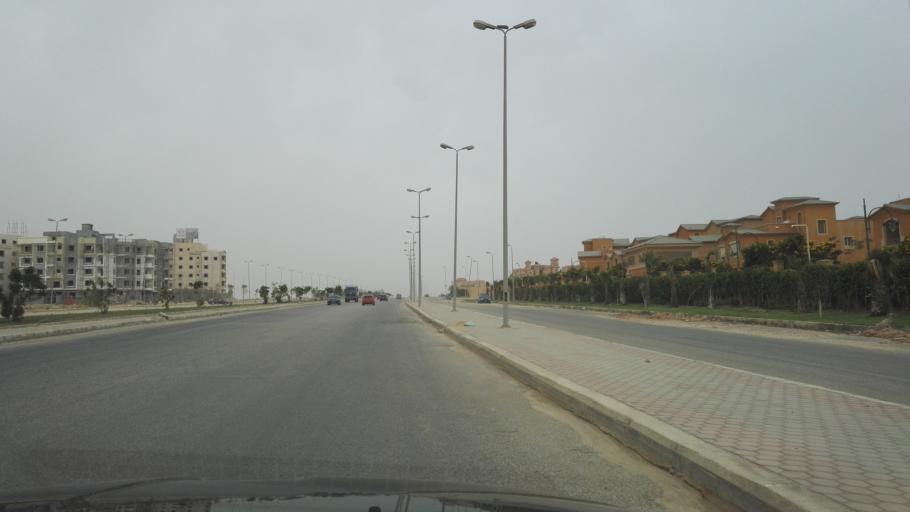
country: EG
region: Muhafazat al Qalyubiyah
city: Al Khankah
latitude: 30.0389
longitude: 31.5180
